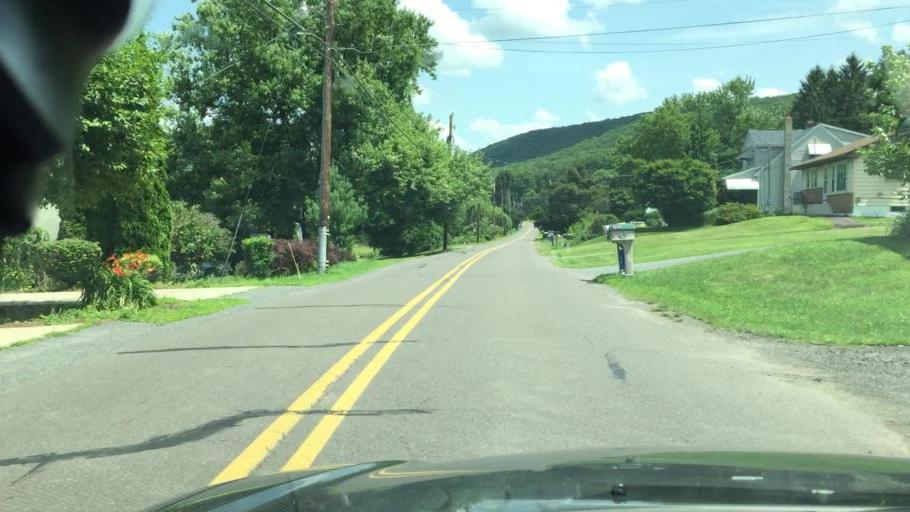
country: US
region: Pennsylvania
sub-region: Luzerne County
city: Harleigh
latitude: 41.0088
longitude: -75.9615
